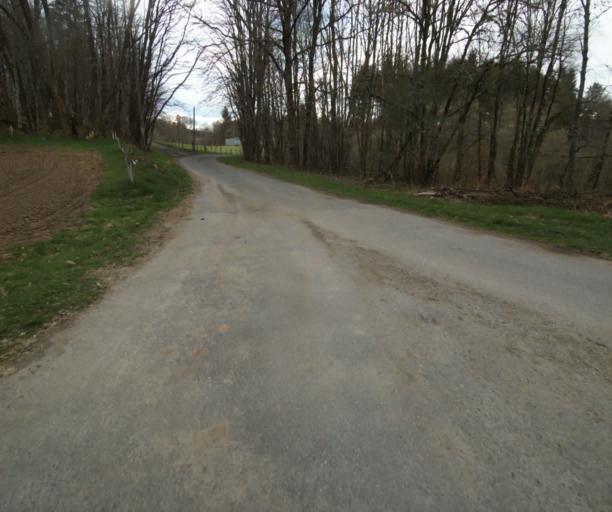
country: FR
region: Limousin
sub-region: Departement de la Correze
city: Correze
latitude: 45.2741
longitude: 1.9512
